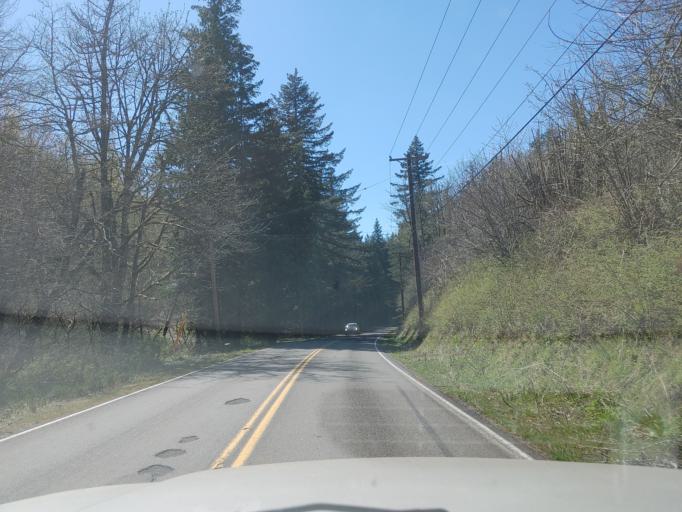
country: US
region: Oregon
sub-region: Multnomah County
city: Troutdale
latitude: 45.5216
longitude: -122.3213
